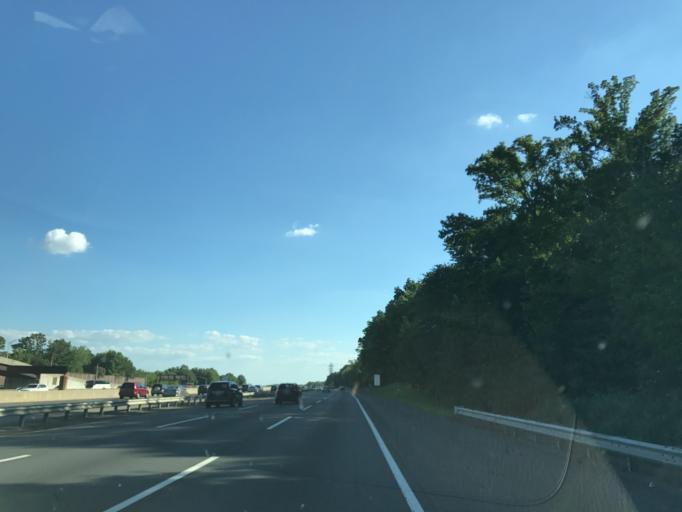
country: US
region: New Jersey
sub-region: Middlesex County
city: East Brunswick
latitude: 40.4232
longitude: -74.4421
